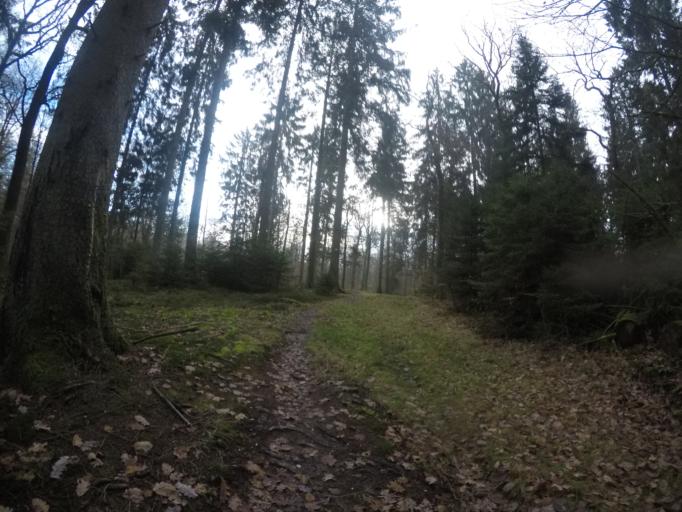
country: BE
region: Wallonia
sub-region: Province du Luxembourg
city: Habay-la-Vieille
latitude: 49.7573
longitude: 5.6004
